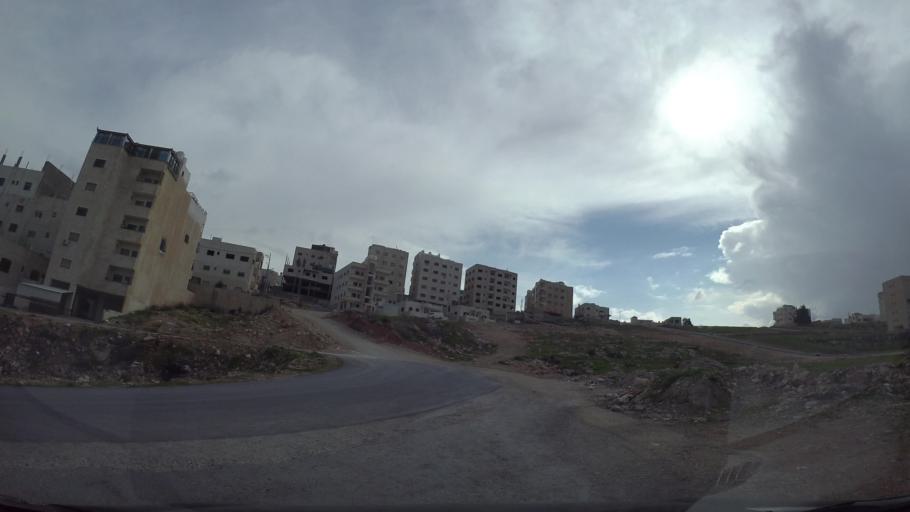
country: JO
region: Amman
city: Amman
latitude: 32.0147
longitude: 35.9427
